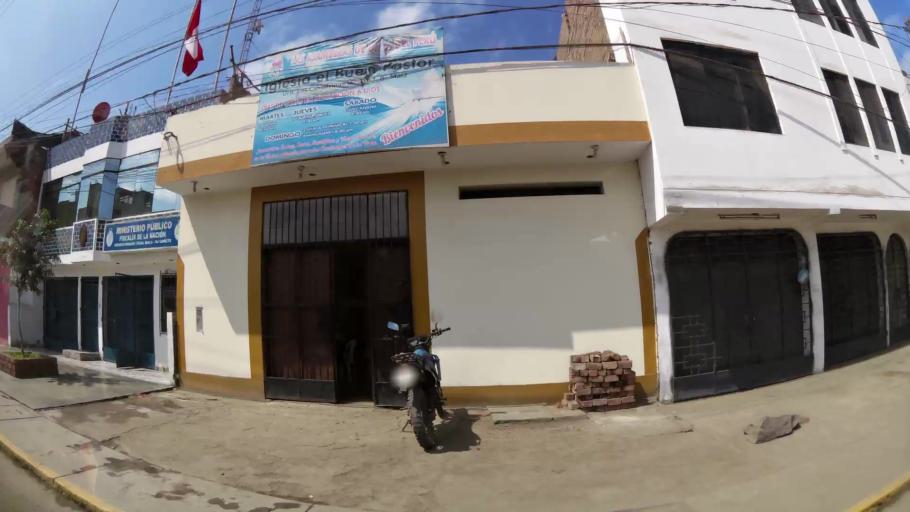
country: PE
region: Lima
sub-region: Provincia de Canete
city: Mala
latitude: -12.6607
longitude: -76.6320
